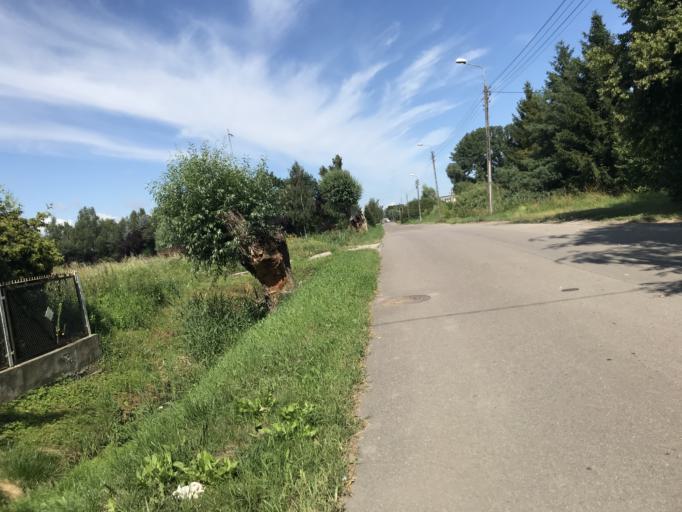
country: PL
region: Pomeranian Voivodeship
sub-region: Gdansk
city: Gdansk
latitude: 54.3308
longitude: 18.6823
